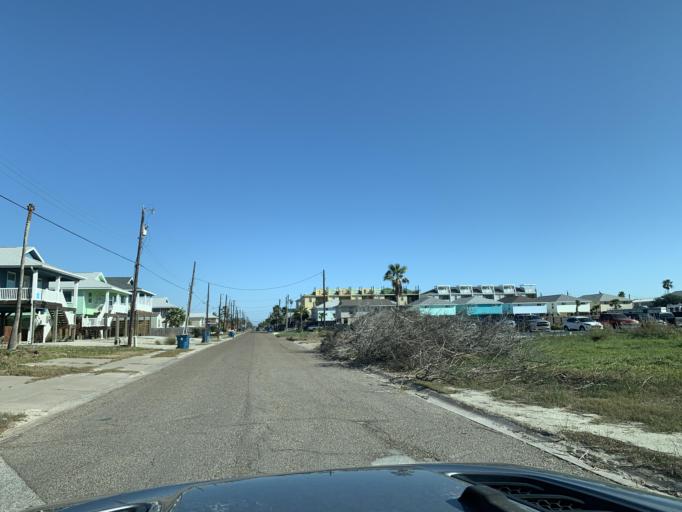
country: US
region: Texas
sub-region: Nueces County
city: Port Aransas
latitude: 27.8180
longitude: -97.0722
